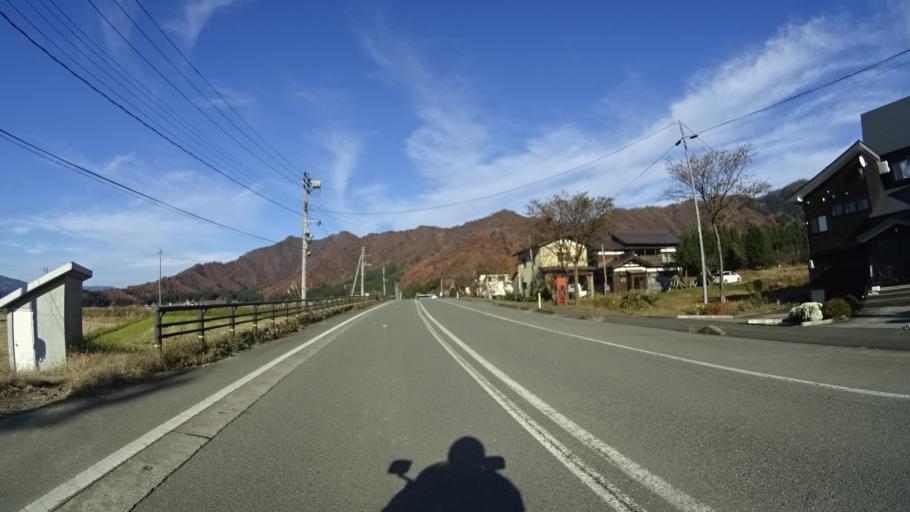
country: JP
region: Niigata
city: Muikamachi
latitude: 37.0346
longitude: 138.8878
